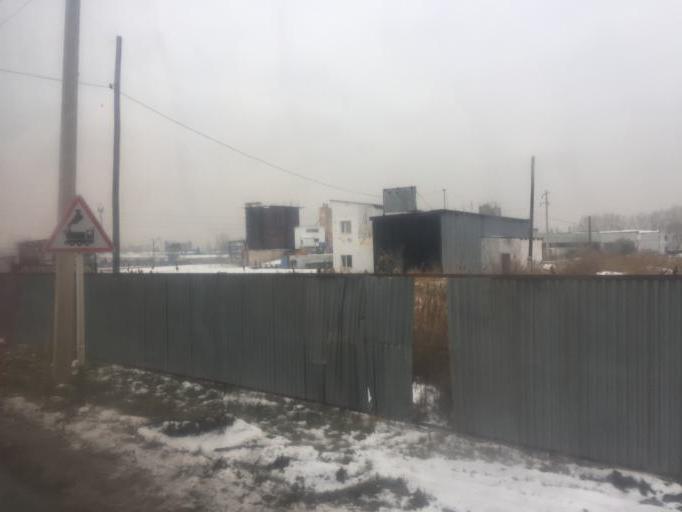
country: KZ
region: Astana Qalasy
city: Astana
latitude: 51.2000
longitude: 71.4105
